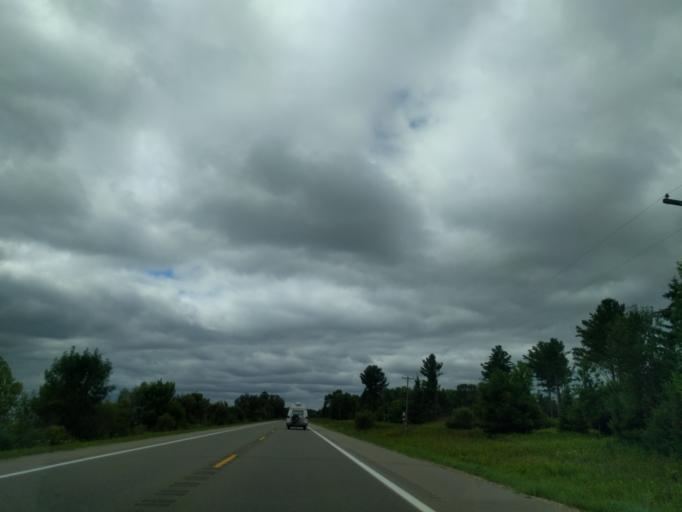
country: US
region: Michigan
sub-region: Menominee County
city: Menominee
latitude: 45.2508
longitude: -87.4873
